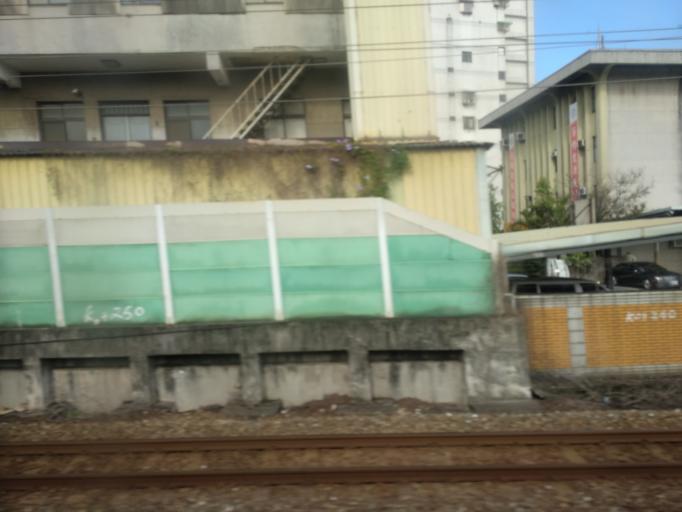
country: TW
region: Taipei
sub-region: Taipei
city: Banqiao
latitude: 24.9872
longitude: 121.4219
